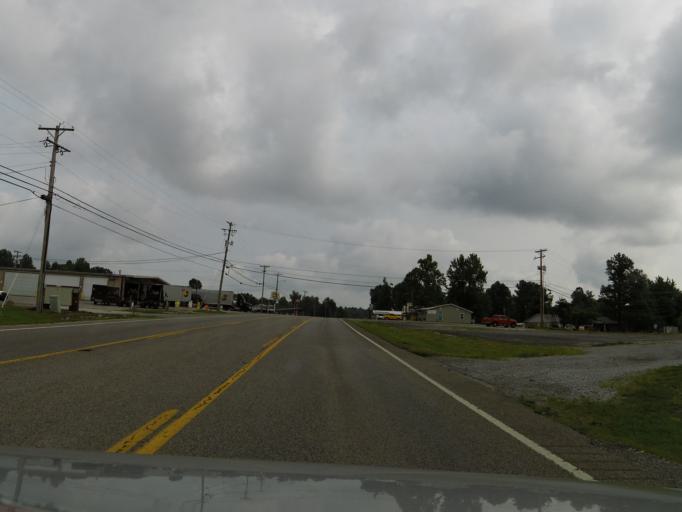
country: US
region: Kentucky
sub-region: Hopkins County
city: Madisonville
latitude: 37.3810
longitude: -87.4888
